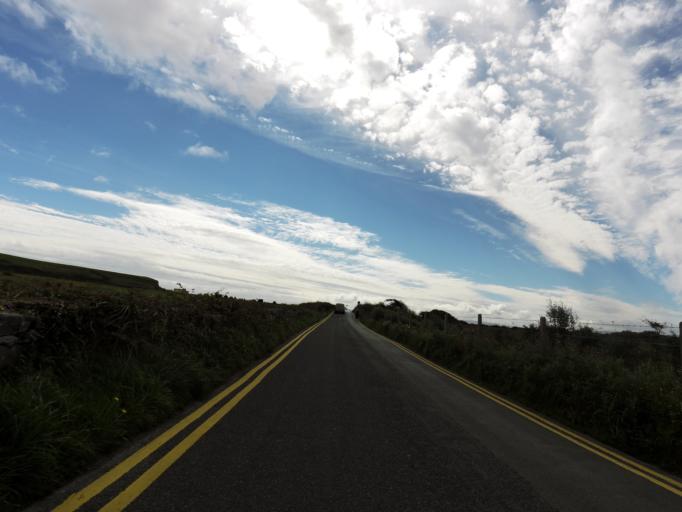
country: IE
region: Connaught
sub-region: County Galway
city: Bearna
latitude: 53.2531
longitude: -9.1294
